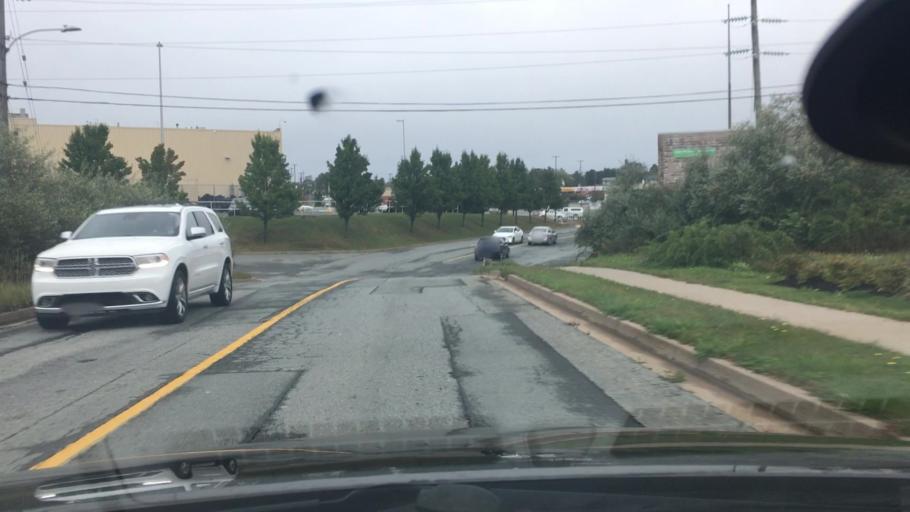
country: CA
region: Nova Scotia
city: Dartmouth
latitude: 44.7716
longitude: -63.6965
